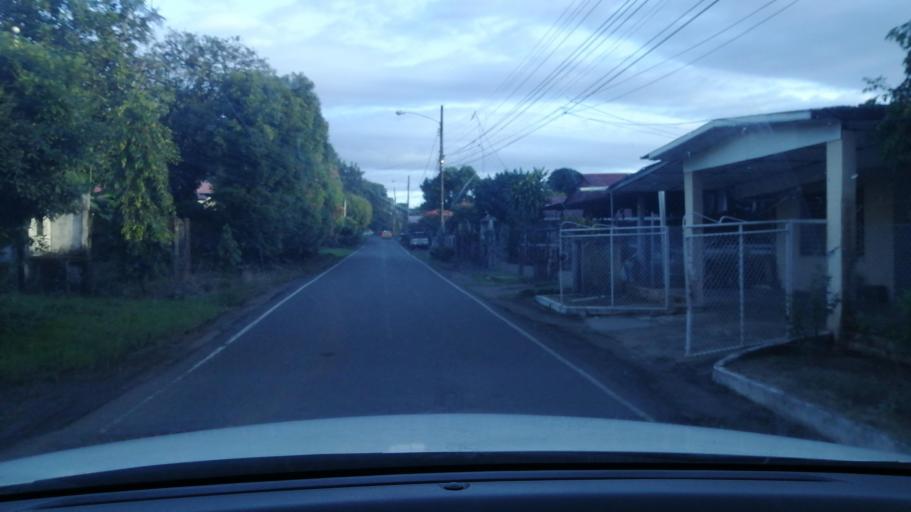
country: PA
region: Chiriqui
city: David
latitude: 8.4134
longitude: -82.4324
